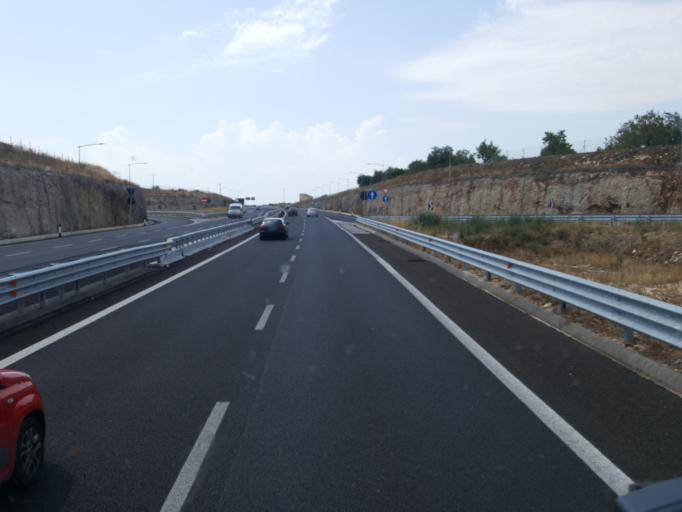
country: IT
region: Apulia
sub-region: Provincia di Bari
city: Palo del Colle
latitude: 41.0458
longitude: 16.7055
